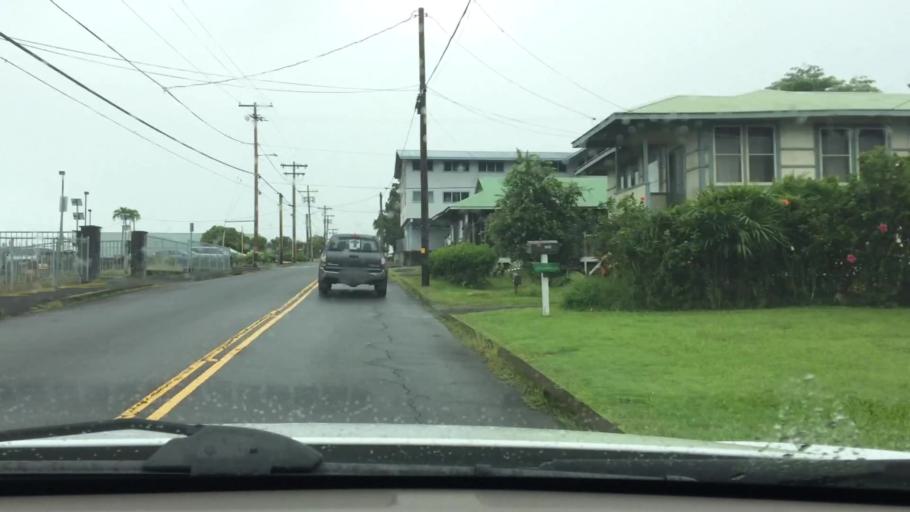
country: US
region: Hawaii
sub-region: Hawaii County
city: Hilo
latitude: 19.7183
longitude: -155.0864
